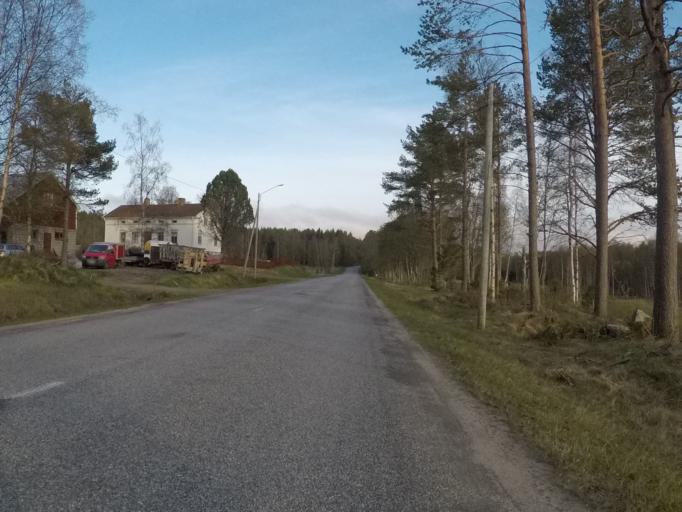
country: SE
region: Vaesterbotten
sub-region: Robertsfors Kommun
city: Robertsfors
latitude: 63.9941
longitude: 20.8084
